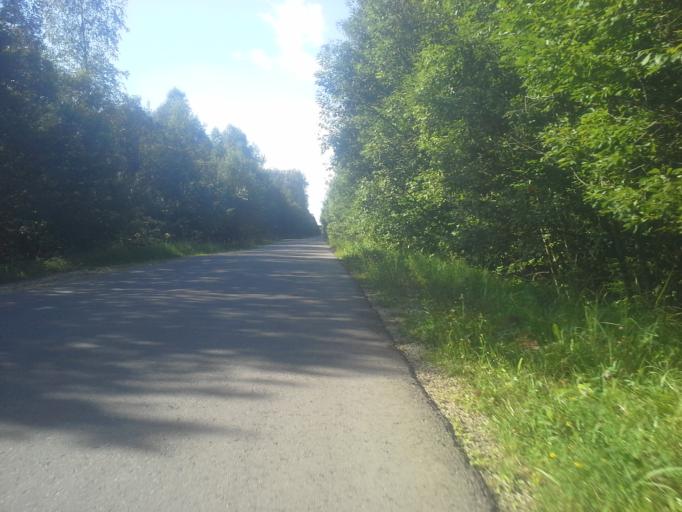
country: RU
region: Moskovskaya
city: Kievskij
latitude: 55.3321
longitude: 36.9884
